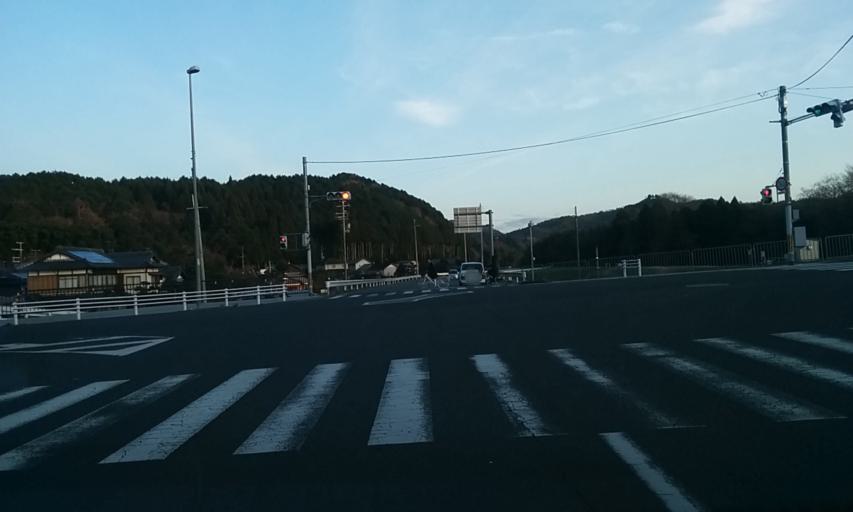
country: JP
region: Kyoto
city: Ayabe
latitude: 35.3116
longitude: 135.2590
